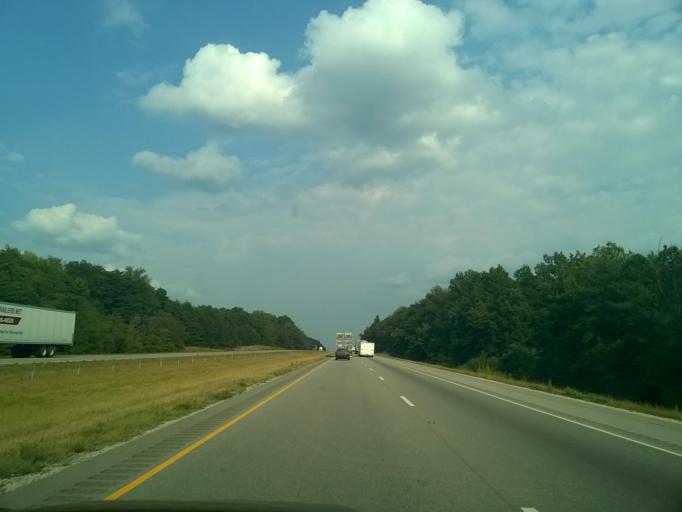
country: US
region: Indiana
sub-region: Clay County
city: Brazil
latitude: 39.4507
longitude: -87.1794
